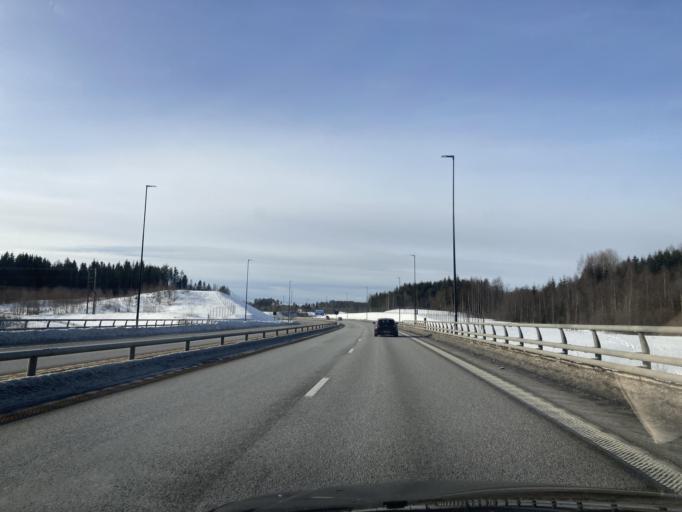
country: NO
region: Hedmark
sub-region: Loten
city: Loten
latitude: 60.8374
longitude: 11.3029
